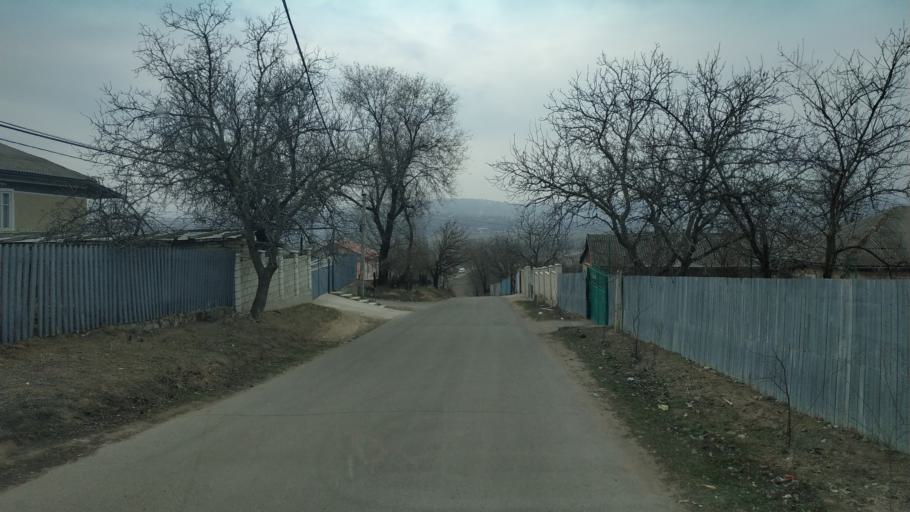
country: MD
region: Chisinau
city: Singera
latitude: 46.9348
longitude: 28.9848
